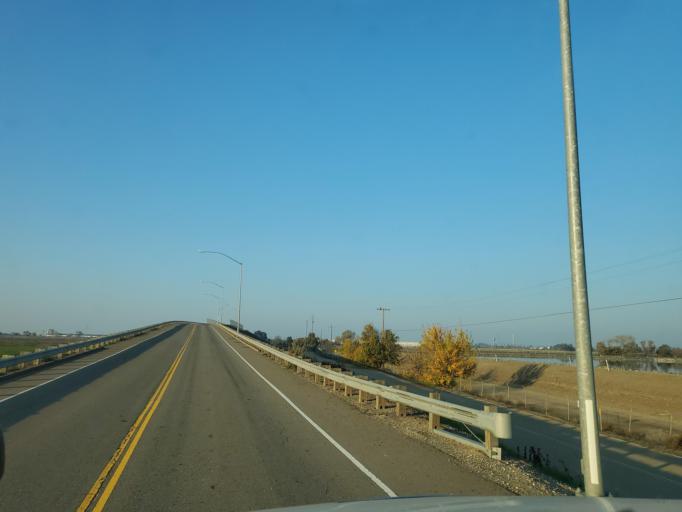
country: US
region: California
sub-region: San Joaquin County
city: Country Club
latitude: 37.9313
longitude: -121.3580
